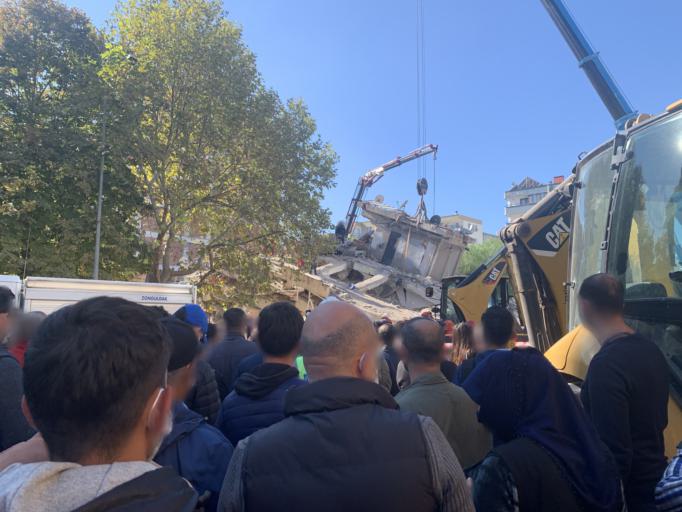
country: TR
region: Izmir
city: Bornova
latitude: 38.4588
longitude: 27.1957
